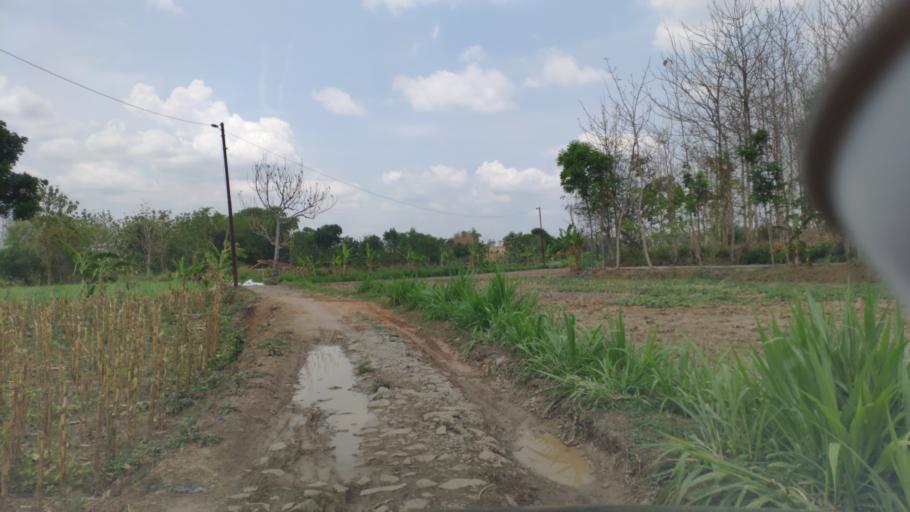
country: ID
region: Central Java
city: Gumiring
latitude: -7.0492
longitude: 111.3952
